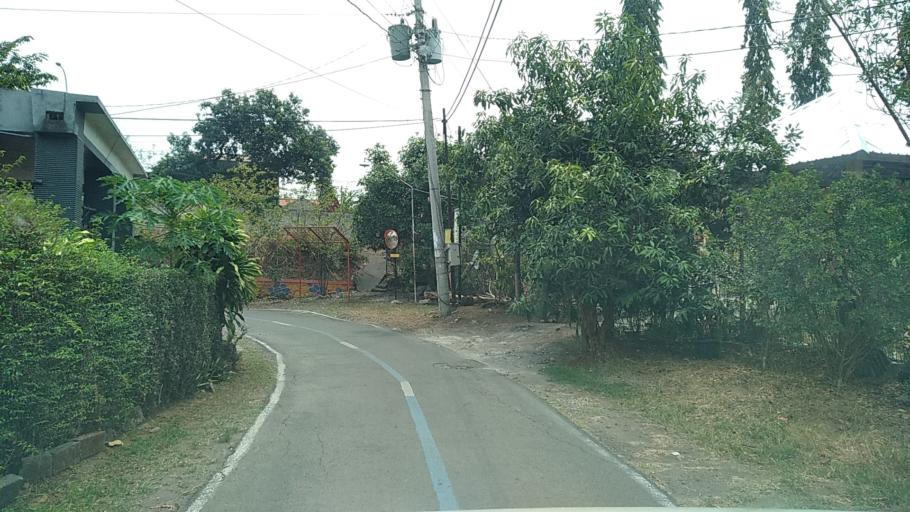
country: ID
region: Central Java
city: Semarang
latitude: -7.0335
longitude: 110.4323
